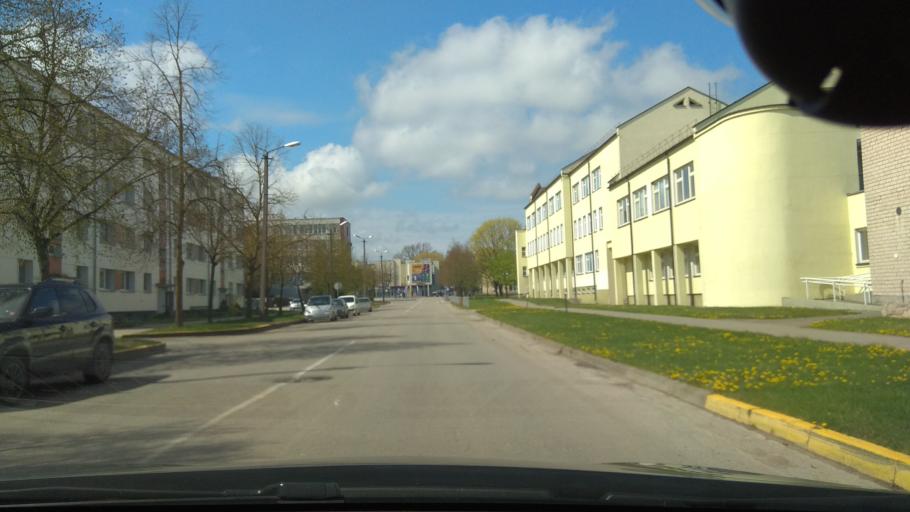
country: LT
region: Siauliu apskritis
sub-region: Joniskis
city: Joniskis
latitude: 56.2425
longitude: 23.6204
